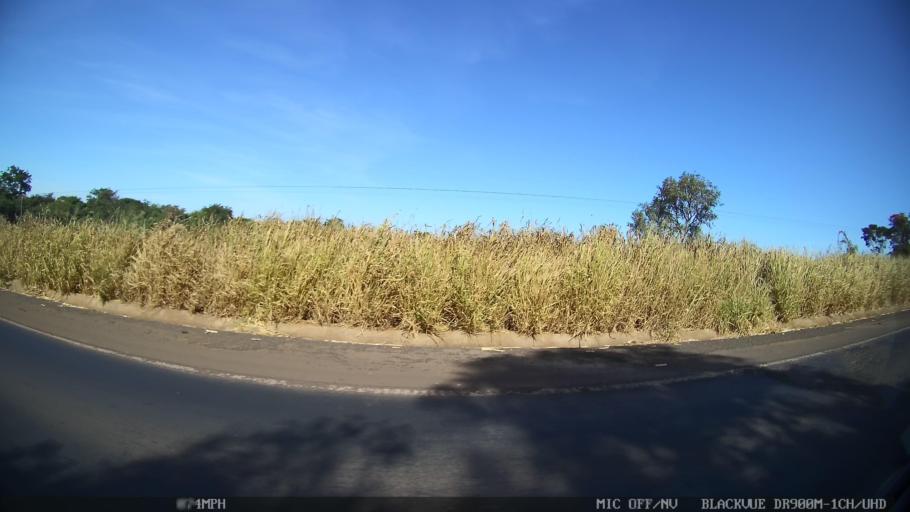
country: BR
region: Sao Paulo
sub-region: Barretos
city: Barretos
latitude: -20.5929
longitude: -48.7121
